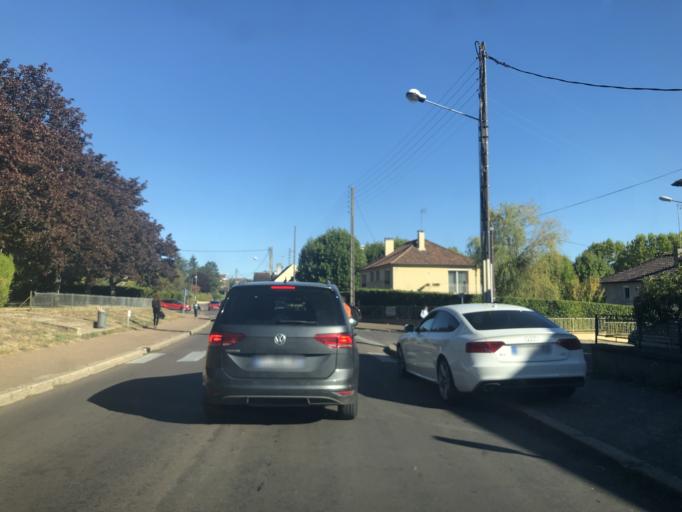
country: FR
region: Bourgogne
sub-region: Departement de l'Yonne
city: Joigny
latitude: 47.9802
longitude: 3.4194
